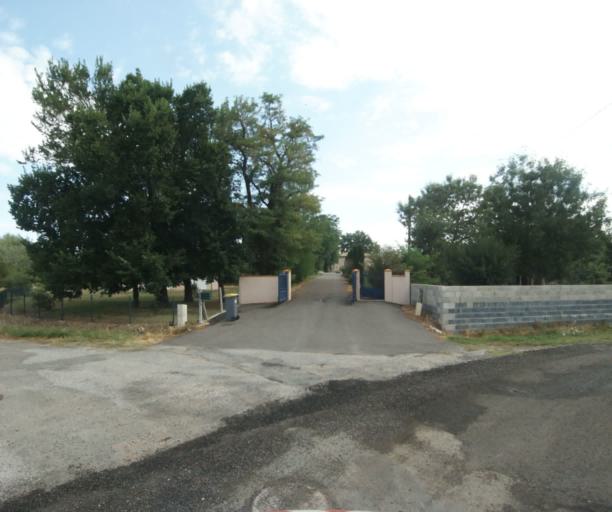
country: FR
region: Midi-Pyrenees
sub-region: Departement de la Haute-Garonne
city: Revel
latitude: 43.4666
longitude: 2.0001
